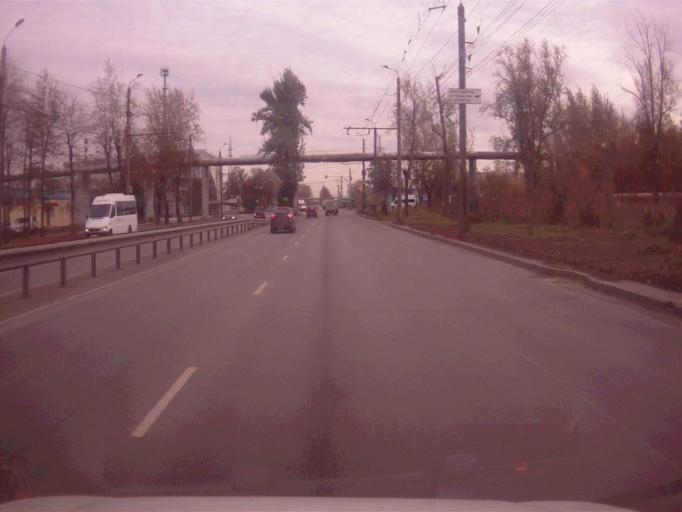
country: RU
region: Chelyabinsk
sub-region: Gorod Chelyabinsk
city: Chelyabinsk
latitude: 55.1347
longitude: 61.4662
